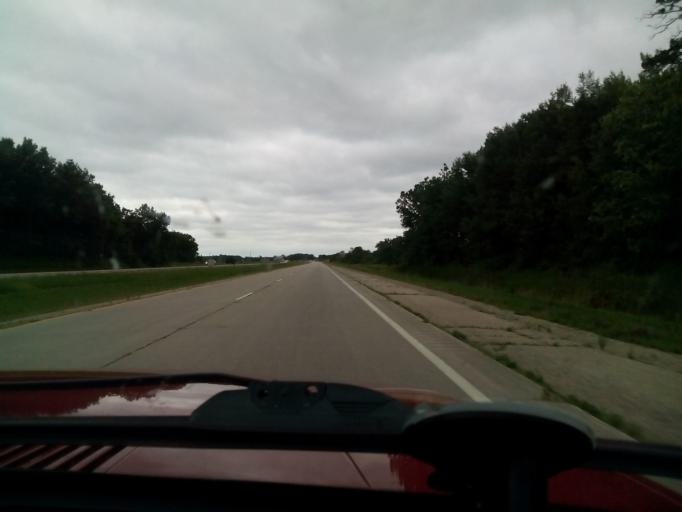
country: US
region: Wisconsin
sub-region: Dane County
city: Marshall
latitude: 43.2601
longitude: -89.1185
